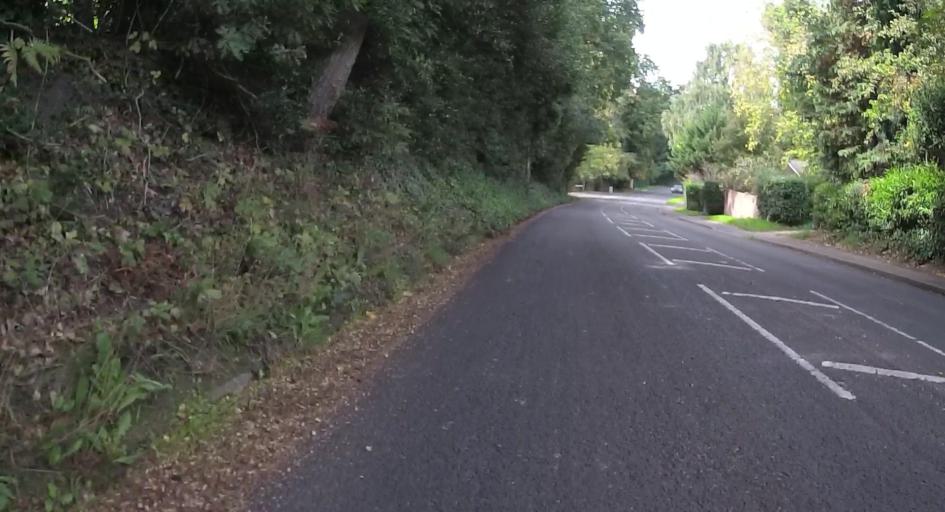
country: GB
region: England
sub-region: Surrey
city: Windlesham
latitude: 51.3478
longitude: -0.6597
